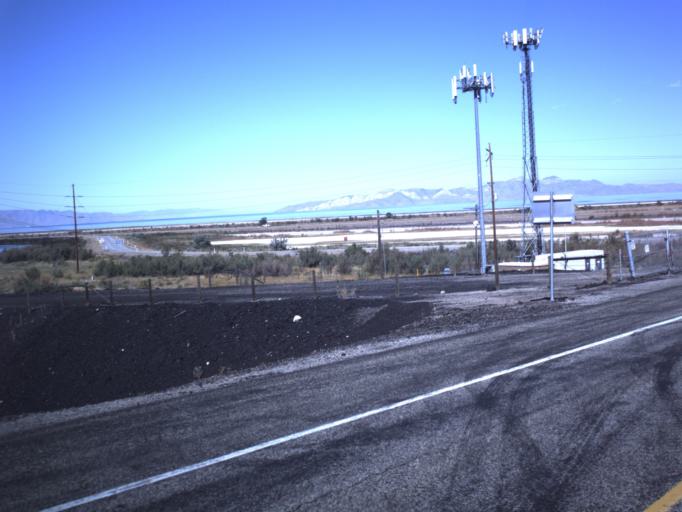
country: US
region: Utah
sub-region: Salt Lake County
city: Magna
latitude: 40.7421
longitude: -112.1791
